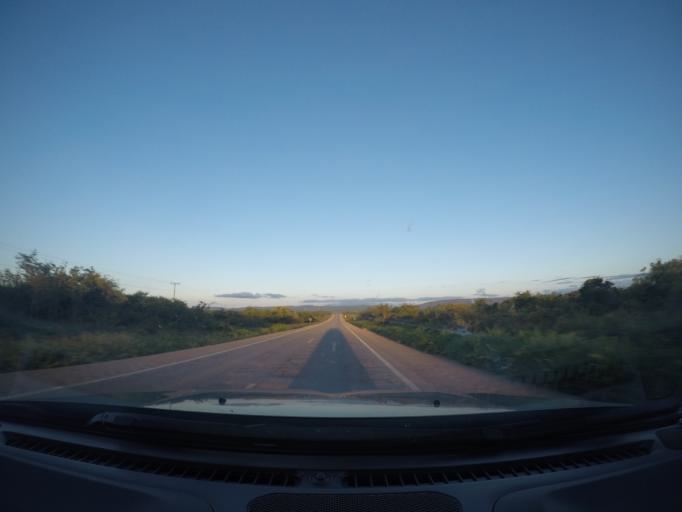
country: BR
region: Bahia
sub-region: Seabra
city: Seabra
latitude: -12.4051
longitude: -41.9560
